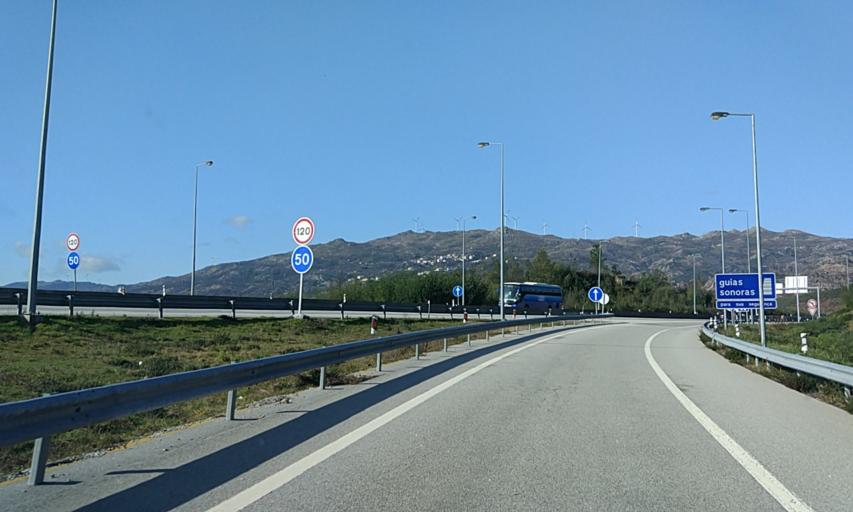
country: PT
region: Viseu
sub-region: Vouzela
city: Vouzela
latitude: 40.6499
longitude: -8.0620
